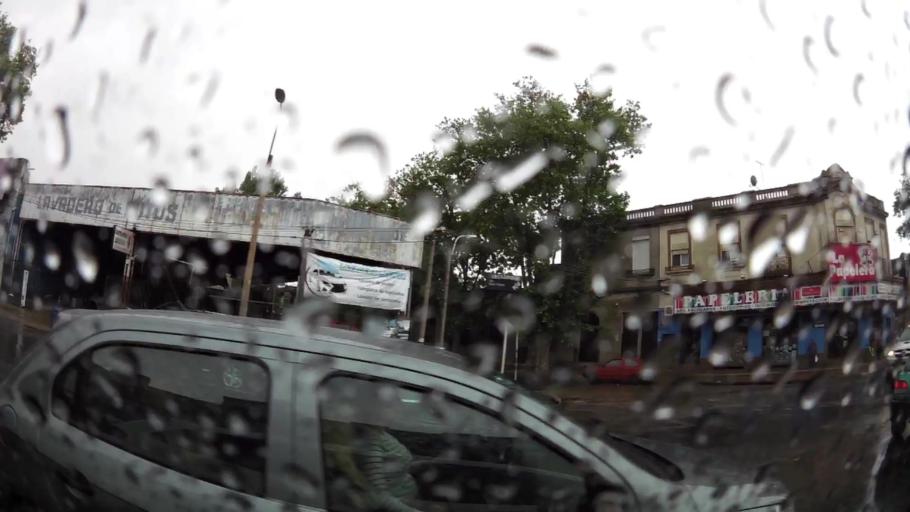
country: UY
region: Montevideo
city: Montevideo
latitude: -34.8744
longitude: -56.1780
